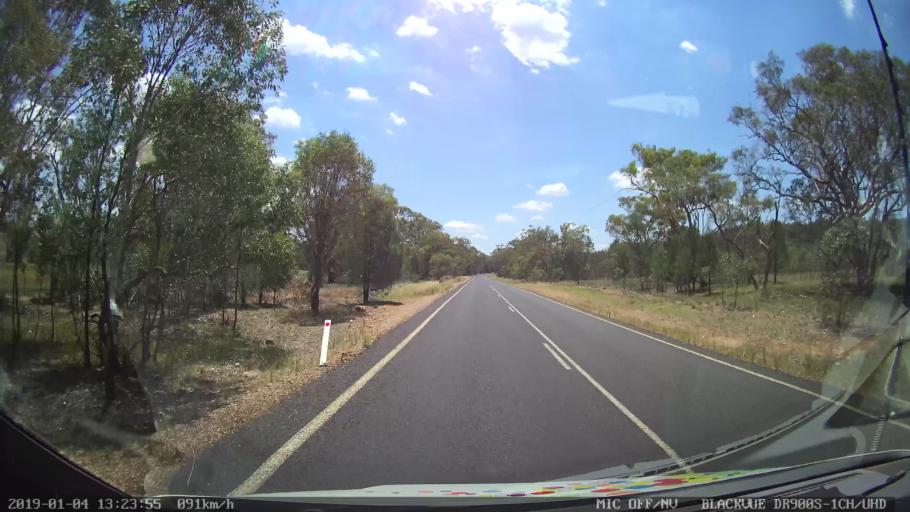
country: AU
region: New South Wales
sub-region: Parkes
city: Peak Hill
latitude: -32.7124
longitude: 148.5517
